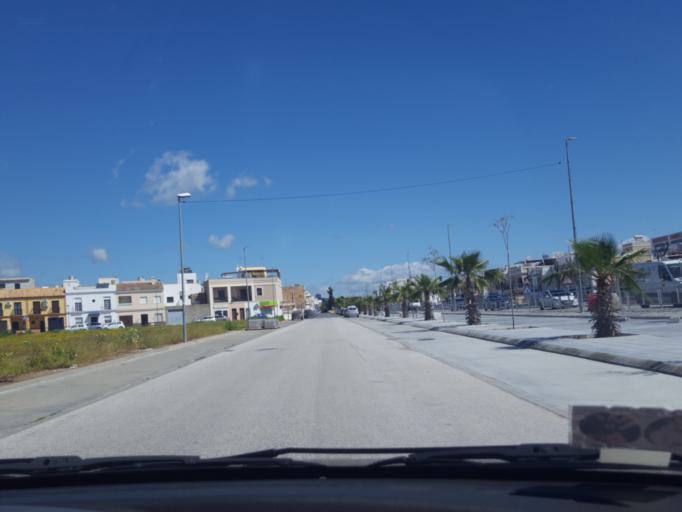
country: ES
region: Andalusia
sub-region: Provincia de Sevilla
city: Acala del Rio
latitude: 37.5170
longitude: -5.9856
